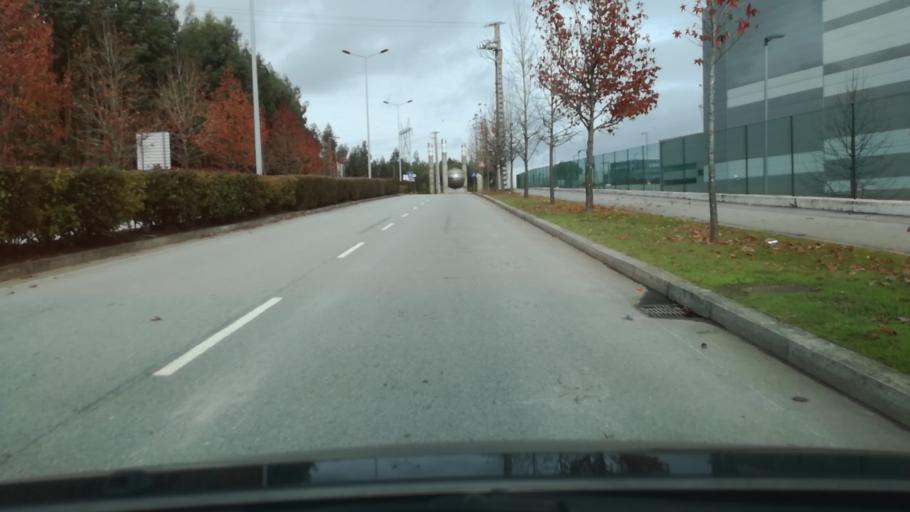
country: PT
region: Porto
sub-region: Maia
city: Maia
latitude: 41.2434
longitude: -8.6304
